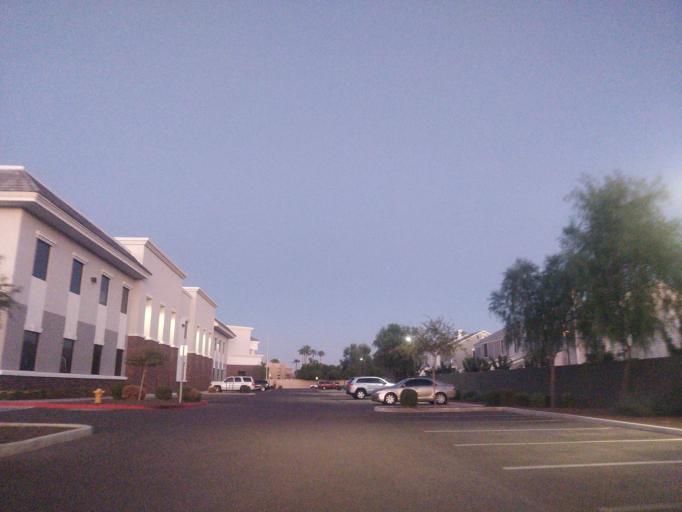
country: US
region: Arizona
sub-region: Maricopa County
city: San Carlos
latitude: 33.3334
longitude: -111.8260
